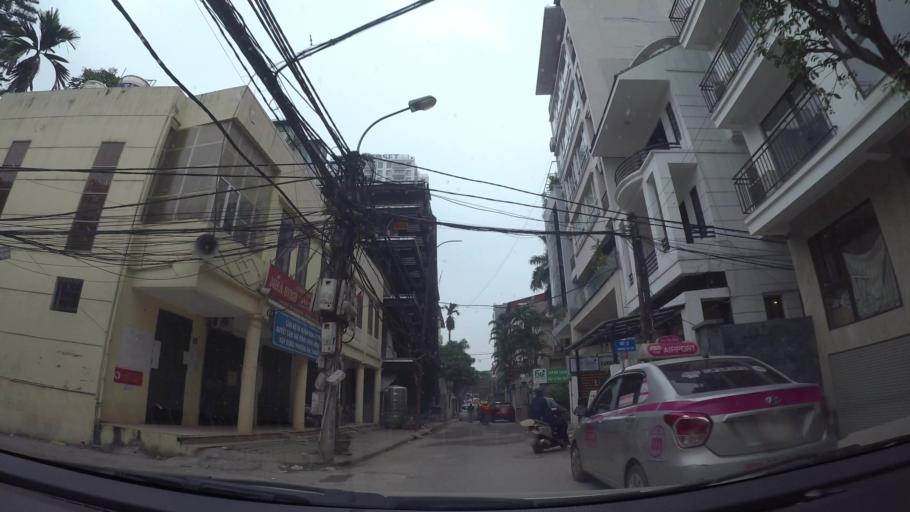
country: VN
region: Ha Noi
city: Tay Ho
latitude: 21.0657
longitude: 105.8249
